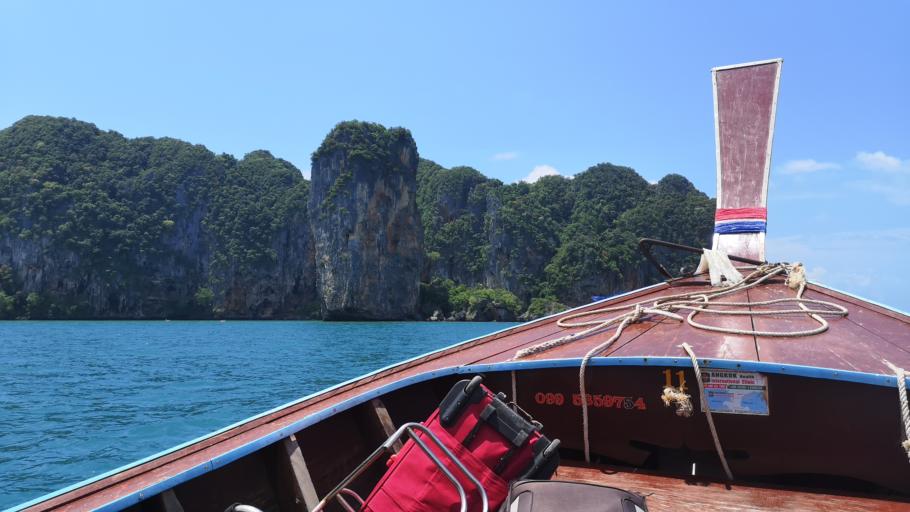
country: TH
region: Phangnga
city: Ban Ao Nang
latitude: 8.0203
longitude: 98.8230
